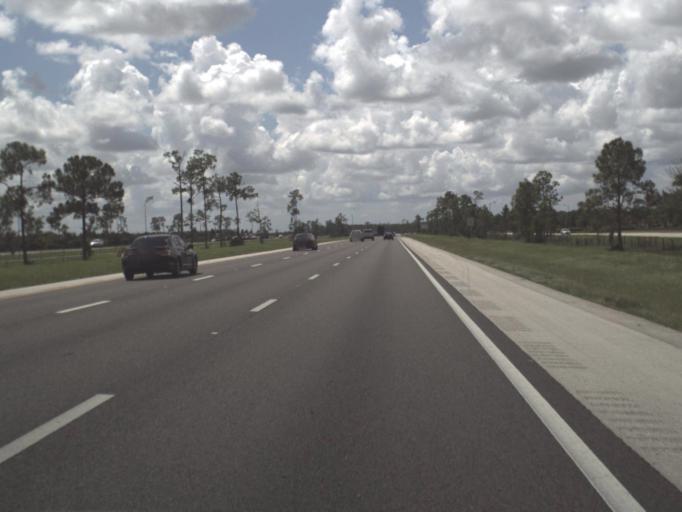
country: US
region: Florida
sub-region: Lee County
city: Bonita Springs
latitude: 26.3837
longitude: -81.7727
